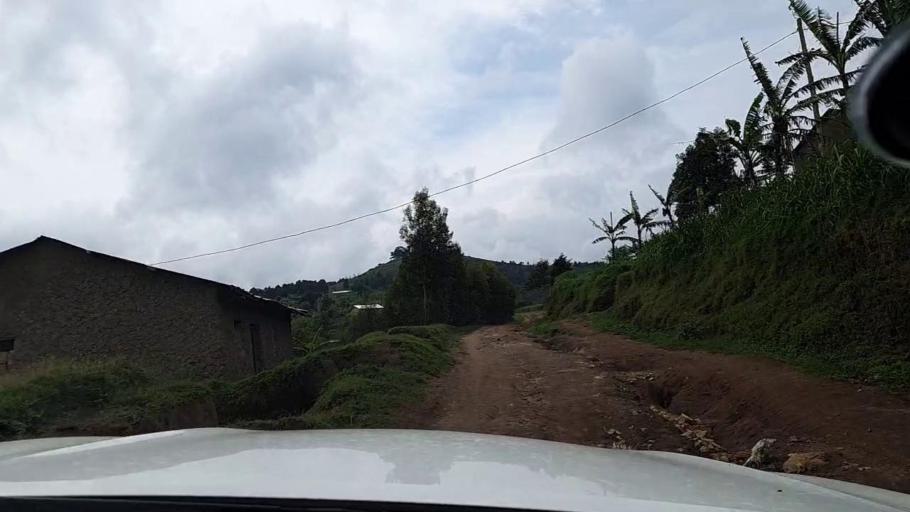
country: RW
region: Western Province
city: Kibuye
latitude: -2.1959
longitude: 29.3184
